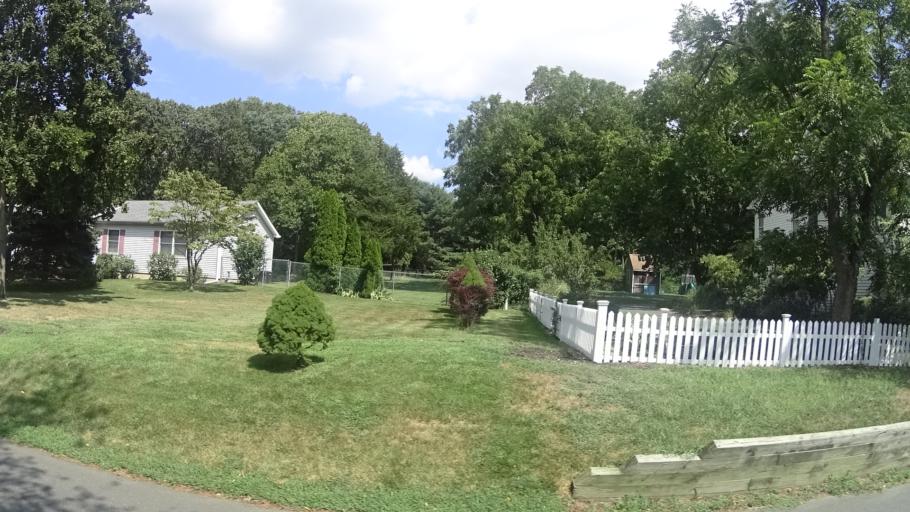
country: US
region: New Jersey
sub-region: Monmouth County
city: Brielle
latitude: 40.1172
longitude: -74.0860
